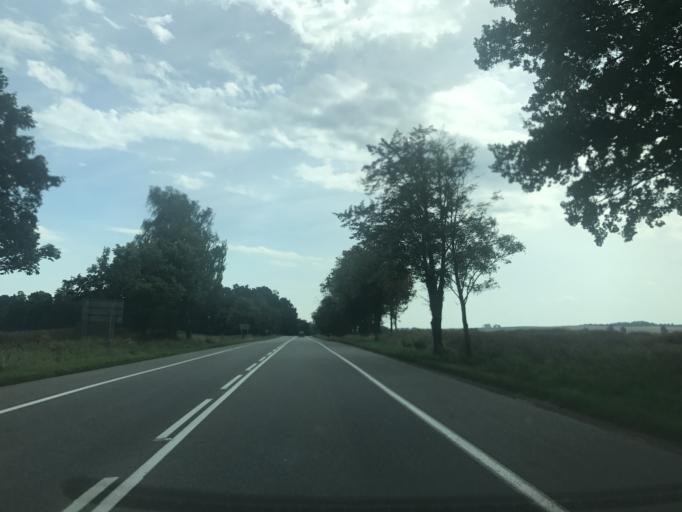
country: PL
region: Warmian-Masurian Voivodeship
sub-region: Powiat ostrodzki
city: Gierzwald
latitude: 53.6305
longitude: 20.0606
